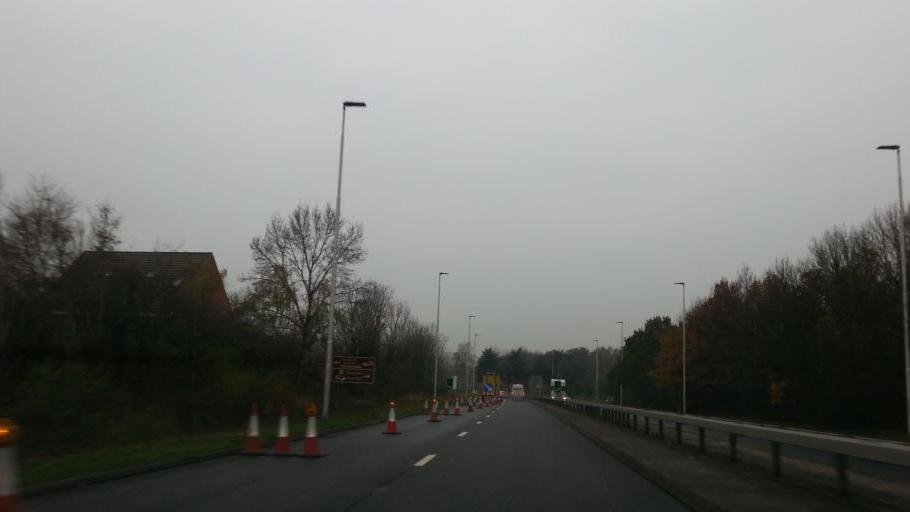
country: GB
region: England
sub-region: Peterborough
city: Castor
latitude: 52.5505
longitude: -0.3109
